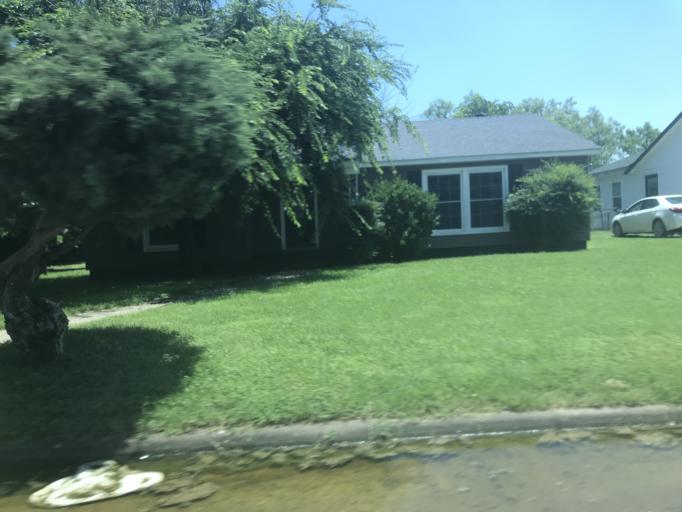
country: US
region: Texas
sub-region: Taylor County
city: Abilene
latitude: 32.4608
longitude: -99.7084
